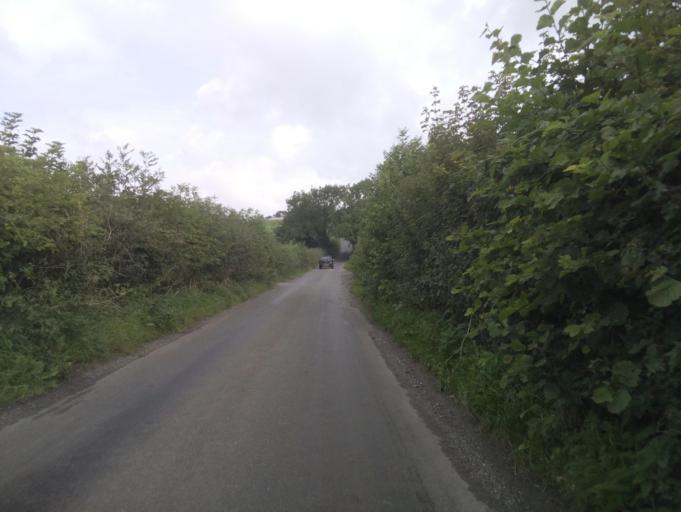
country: GB
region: England
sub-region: Somerset
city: Evercreech
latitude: 51.1567
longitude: -2.5003
